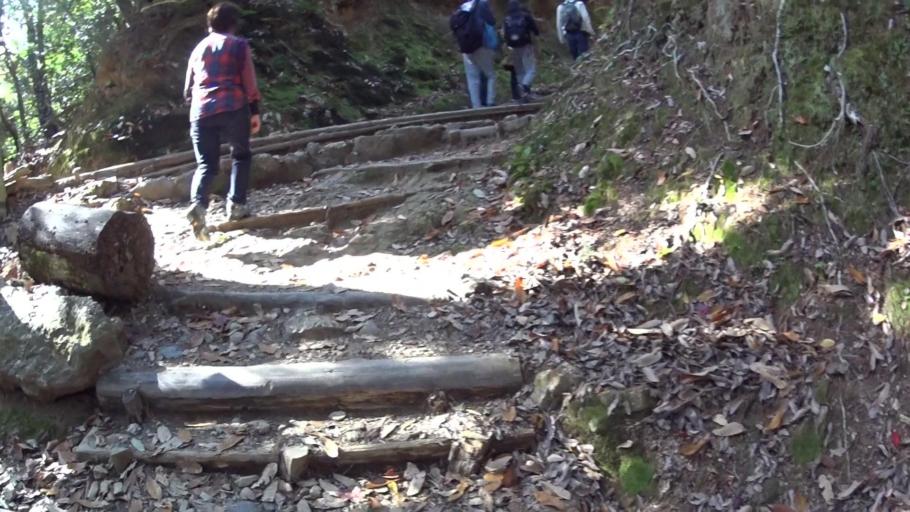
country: JP
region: Kyoto
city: Kameoka
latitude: 35.0416
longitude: 135.6530
